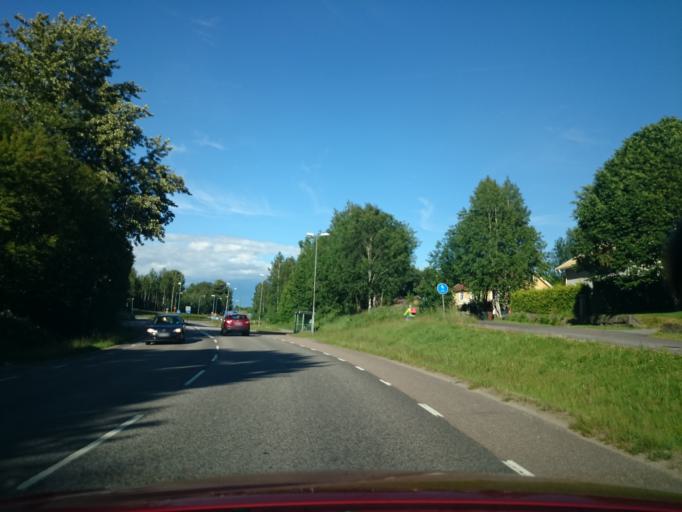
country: SE
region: Vaestra Goetaland
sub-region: Lerums Kommun
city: Lerum
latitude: 57.7768
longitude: 12.2833
